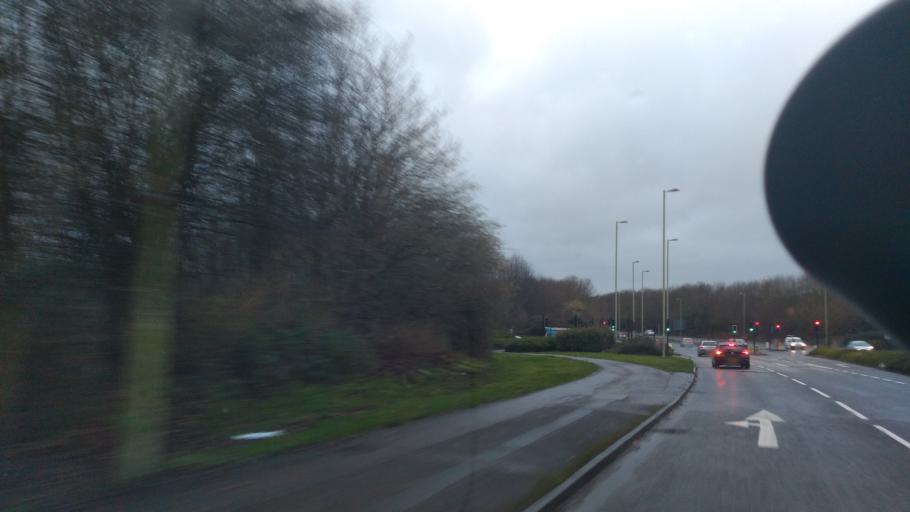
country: GB
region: England
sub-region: Borough of Swindon
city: Broad Blunsdon
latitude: 51.6010
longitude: -1.7952
